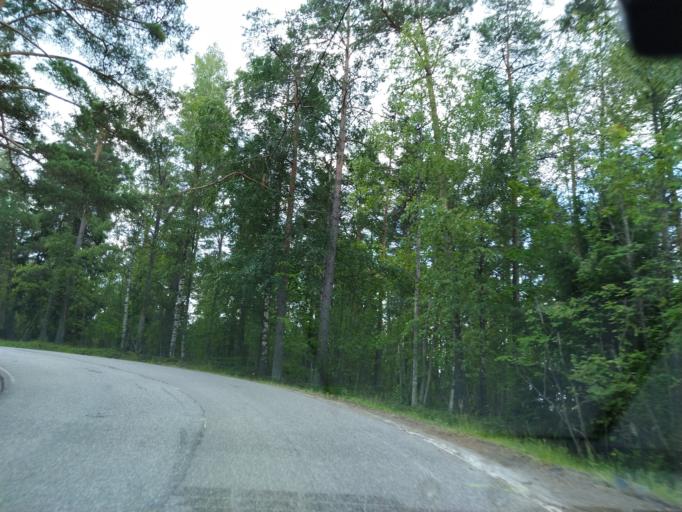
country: FI
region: Uusimaa
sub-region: Helsinki
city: Kirkkonummi
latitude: 60.0969
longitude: 24.4982
